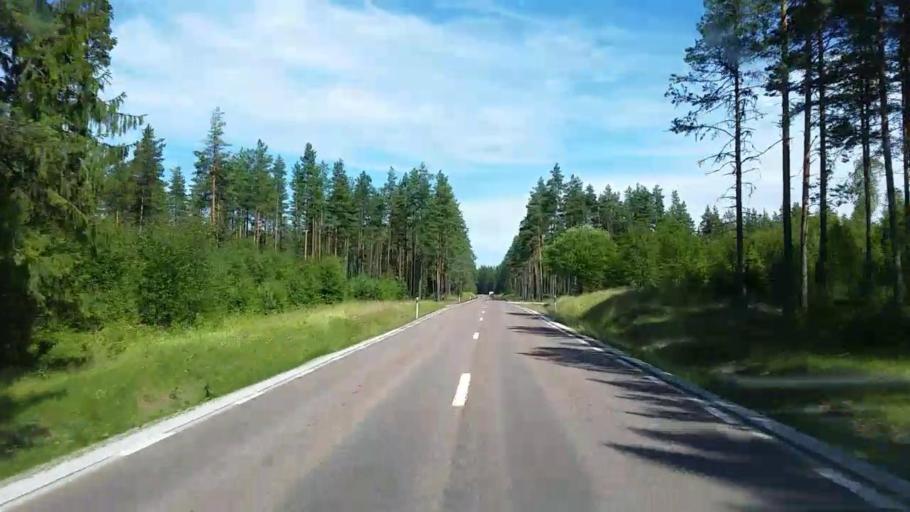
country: SE
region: Dalarna
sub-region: Rattviks Kommun
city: Raettvik
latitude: 60.9067
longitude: 15.1937
